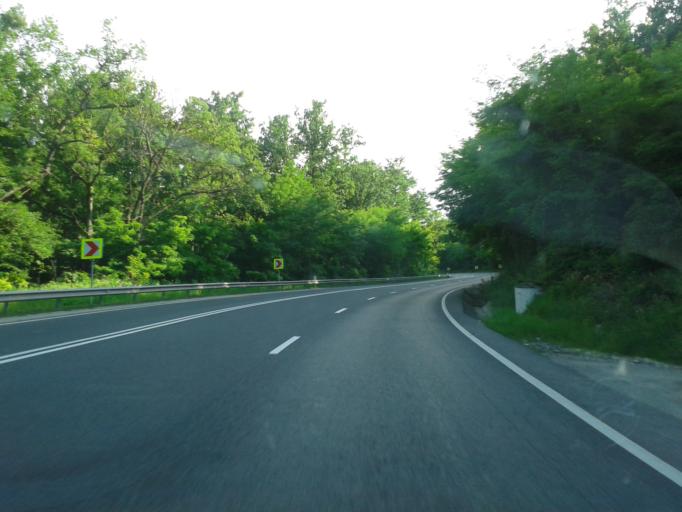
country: RO
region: Hunedoara
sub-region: Oras Hateg
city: Hateg
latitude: 45.6223
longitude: 22.9868
